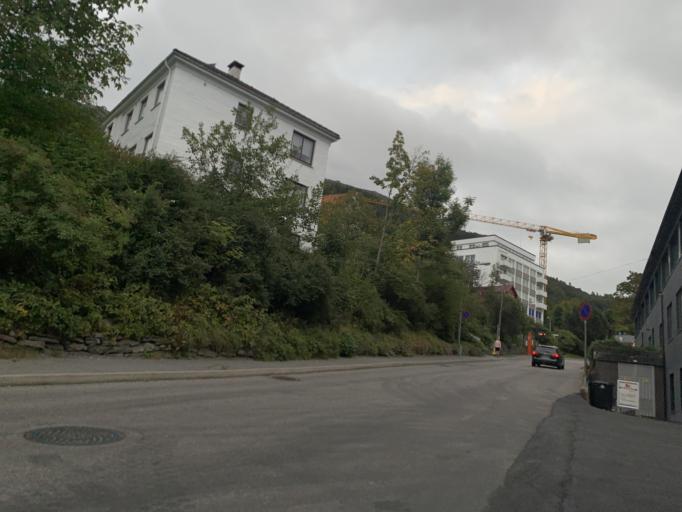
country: NO
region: Hordaland
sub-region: Bergen
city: Bergen
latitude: 60.3777
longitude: 5.3563
